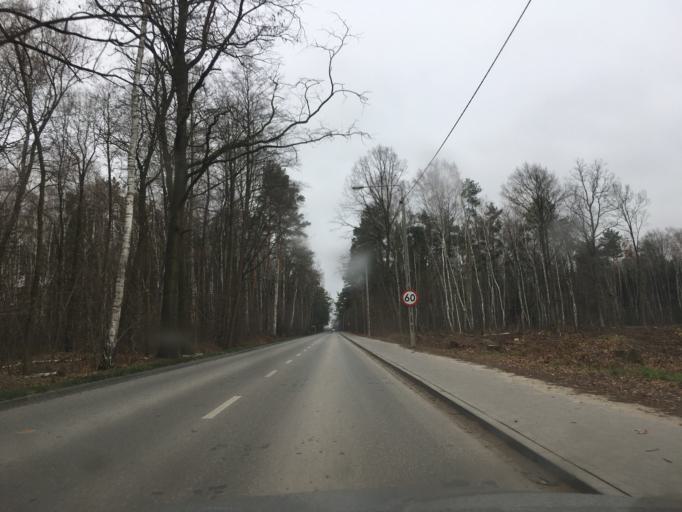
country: PL
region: Masovian Voivodeship
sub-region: Powiat piaseczynski
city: Lesznowola
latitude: 52.0776
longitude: 20.9369
